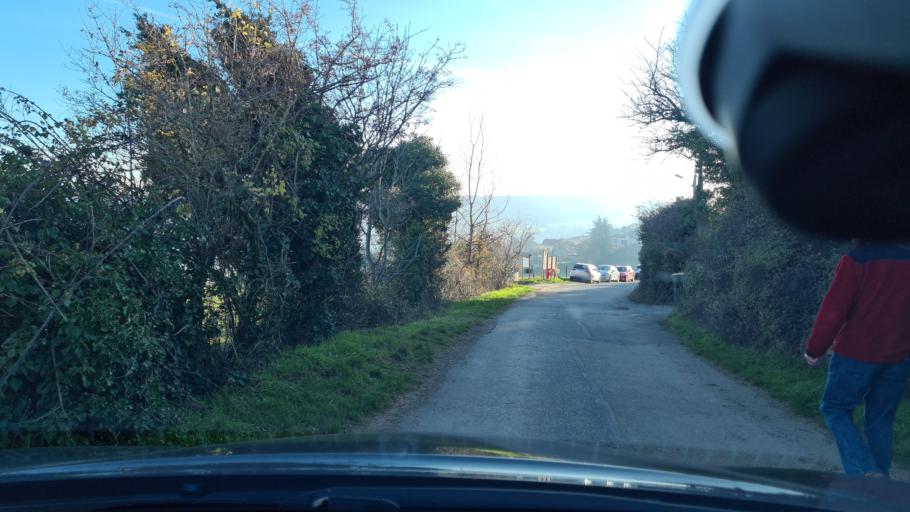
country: FR
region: Rhone-Alpes
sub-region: Departement du Rhone
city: Chasselay
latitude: 45.8656
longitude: 4.7991
